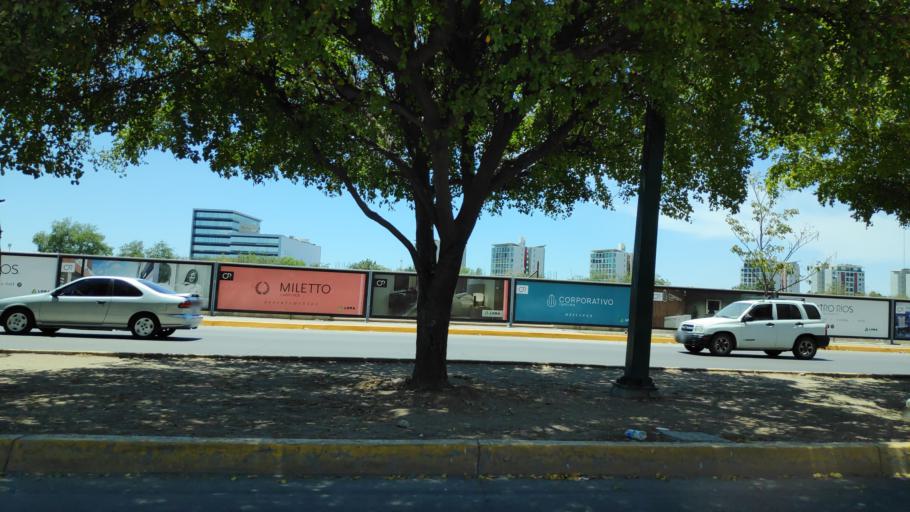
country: MX
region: Sinaloa
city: Culiacan
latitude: 24.8238
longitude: -107.3995
